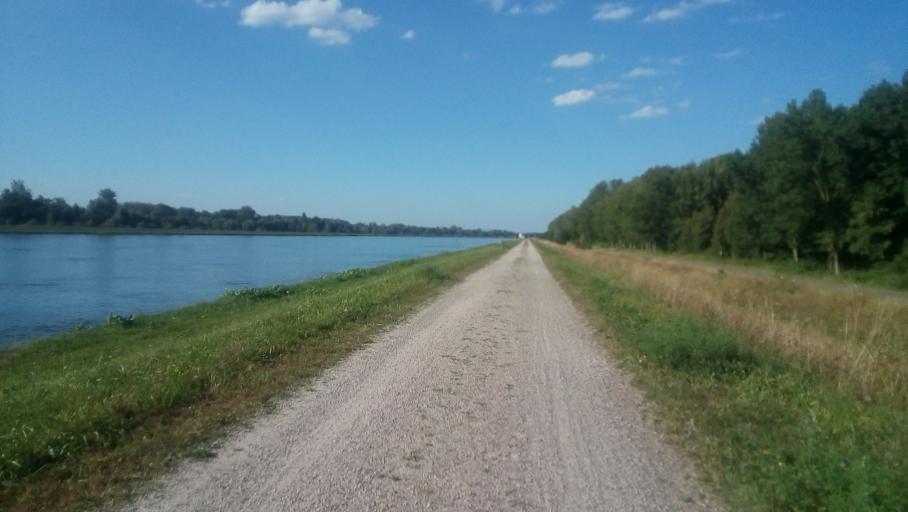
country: DE
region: Baden-Wuerttemberg
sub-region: Karlsruhe Region
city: Lichtenau
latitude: 48.7316
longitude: 7.9696
